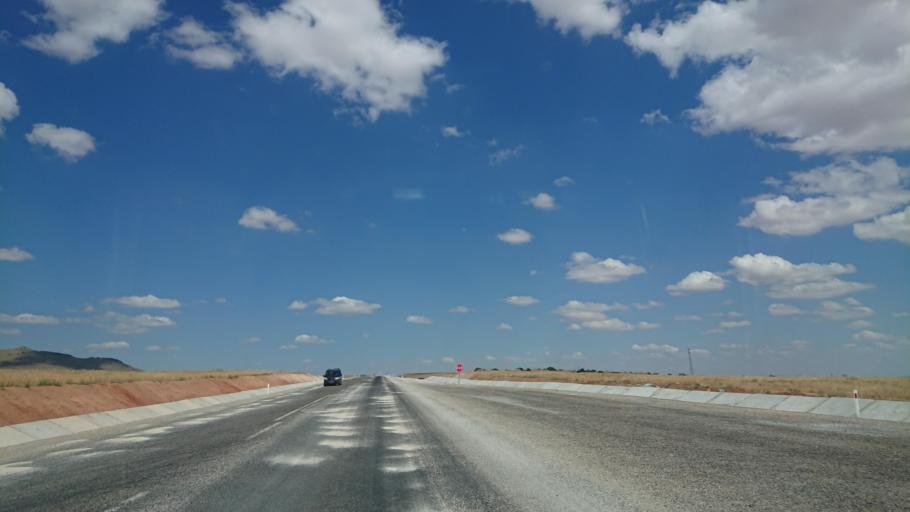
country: TR
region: Kirsehir
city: Kirsehir
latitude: 39.1238
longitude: 33.9766
